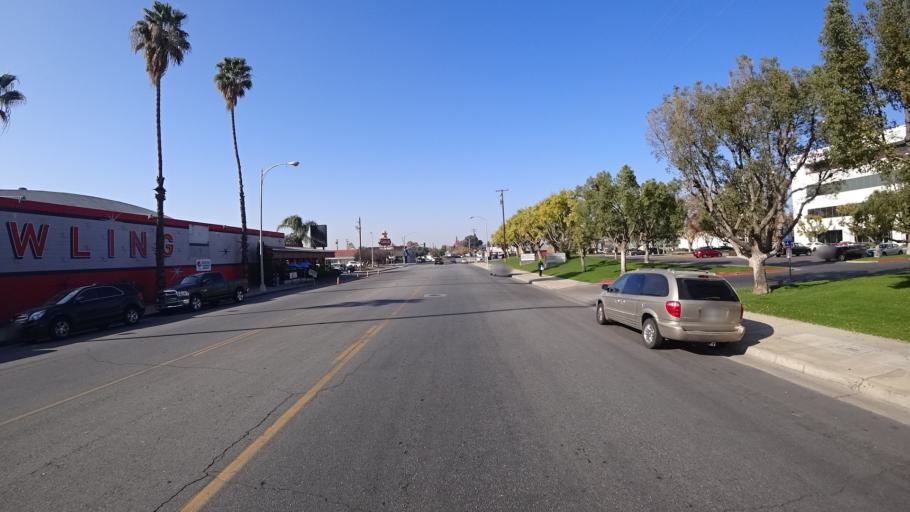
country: US
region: California
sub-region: Kern County
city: Bakersfield
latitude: 35.3868
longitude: -119.0221
